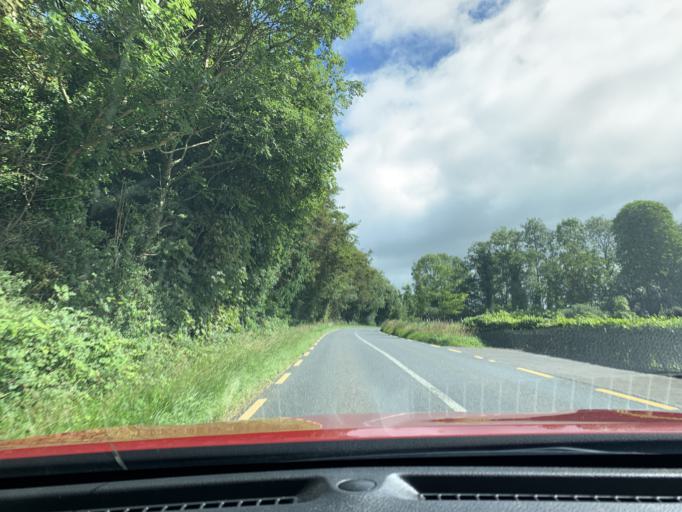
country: IE
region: Connaught
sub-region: Roscommon
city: Boyle
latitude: 53.8415
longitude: -8.2135
